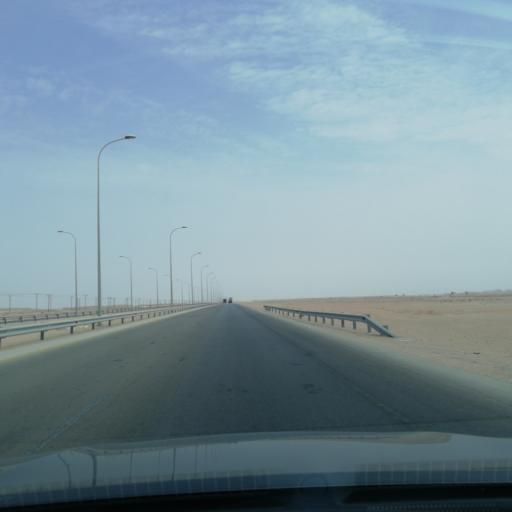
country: OM
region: Zufar
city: Salalah
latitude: 17.5402
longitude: 54.0547
